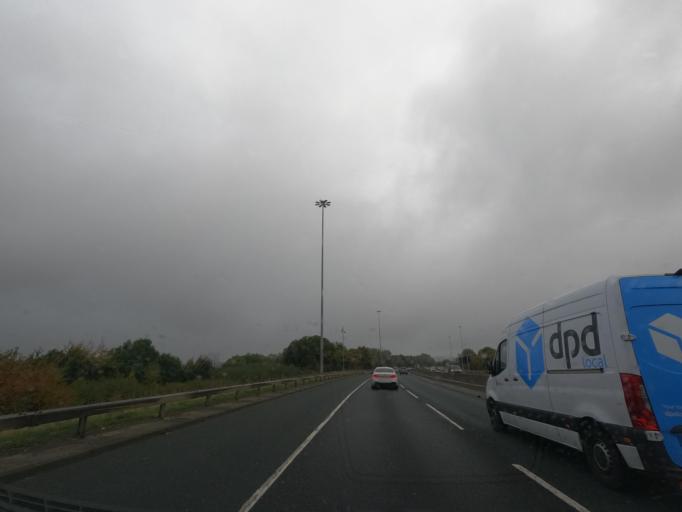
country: GB
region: England
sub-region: Middlesbrough
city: Middlesbrough
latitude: 54.5728
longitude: -1.2561
